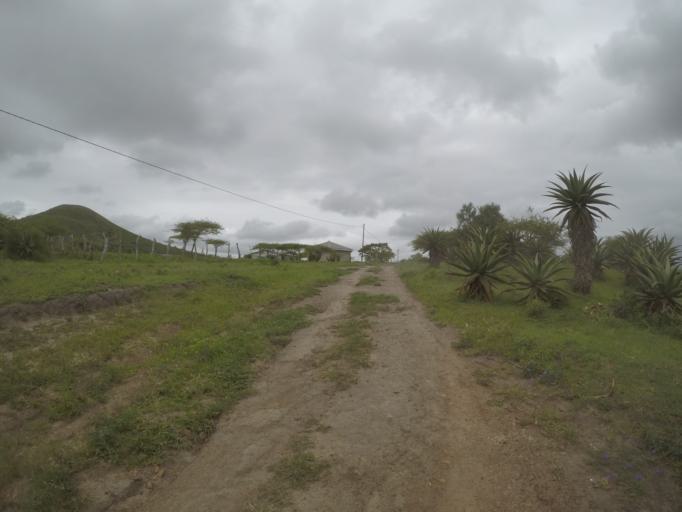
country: ZA
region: KwaZulu-Natal
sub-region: uThungulu District Municipality
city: Empangeni
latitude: -28.5960
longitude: 31.8506
